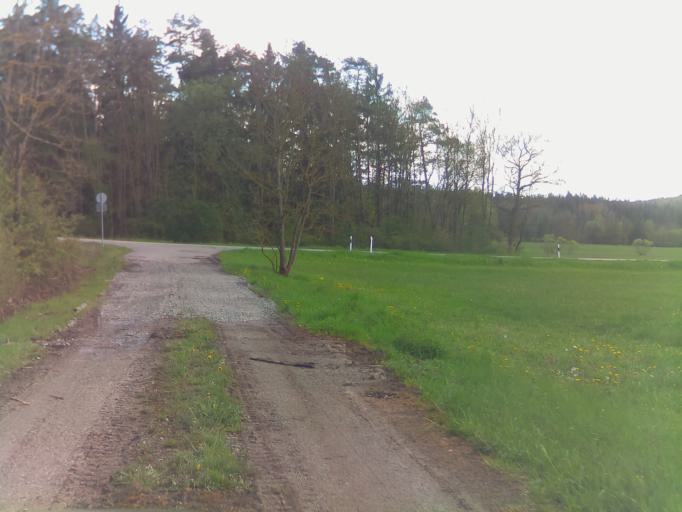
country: DE
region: Bavaria
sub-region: Regierungsbezirk Unterfranken
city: Hochheim
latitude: 50.4064
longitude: 10.4443
